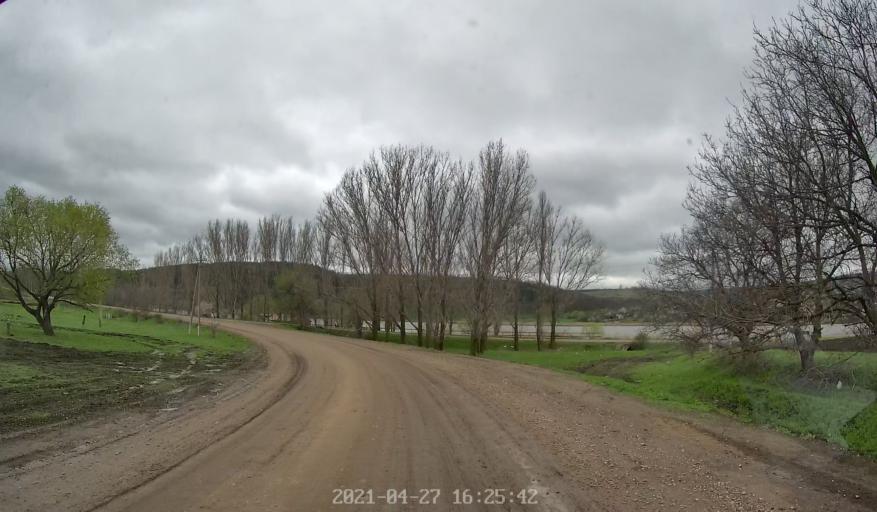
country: MD
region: Chisinau
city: Singera
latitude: 46.9835
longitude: 29.0216
